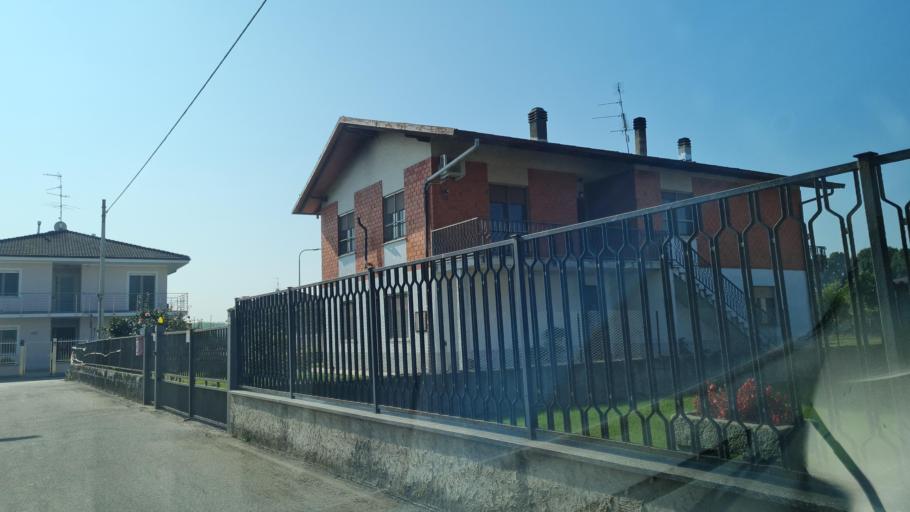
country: IT
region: Piedmont
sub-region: Provincia di Novara
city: Landiona
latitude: 45.4952
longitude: 8.4213
